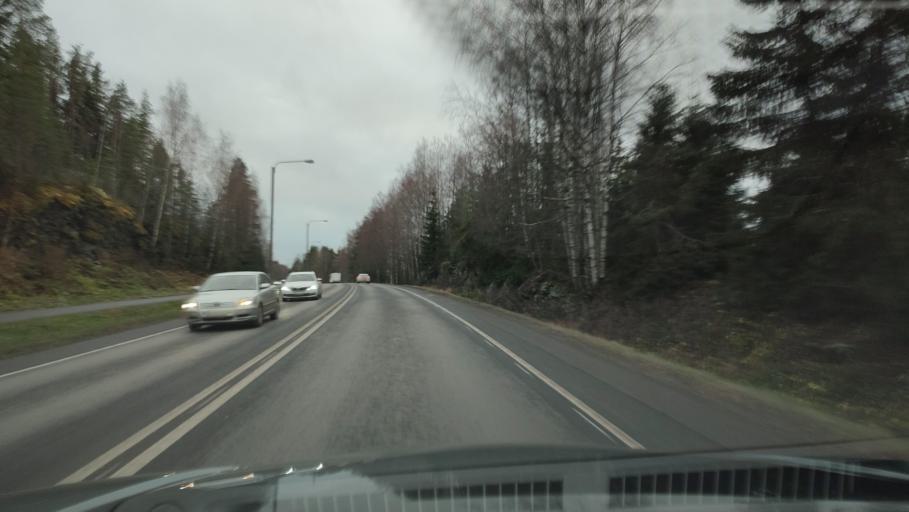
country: FI
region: Southern Ostrobothnia
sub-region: Seinaejoki
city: Seinaejoki
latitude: 62.7909
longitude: 22.7335
